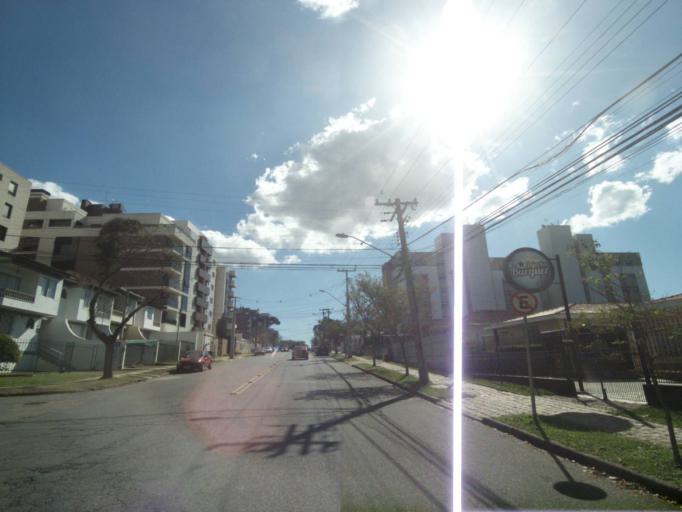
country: BR
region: Parana
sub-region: Curitiba
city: Curitiba
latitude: -25.3994
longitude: -49.2534
